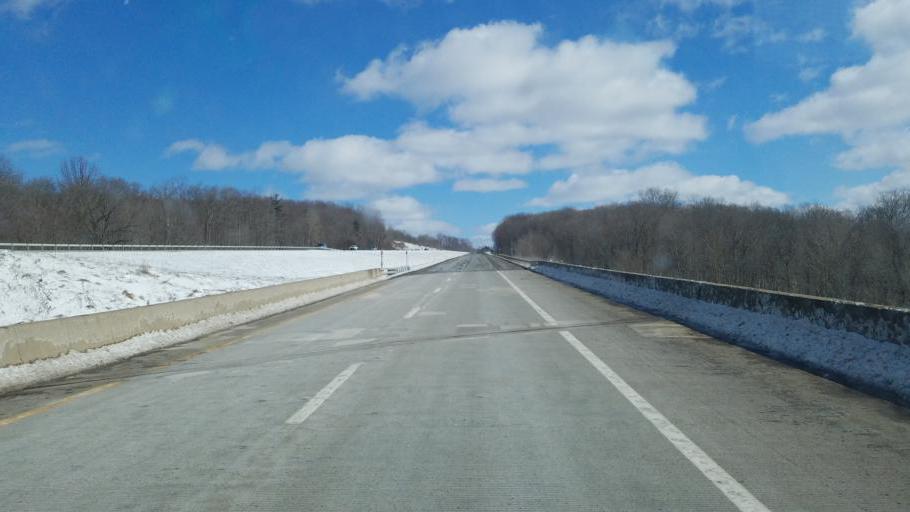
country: US
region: New York
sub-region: Chautauqua County
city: Lakewood
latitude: 42.1375
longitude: -79.3452
